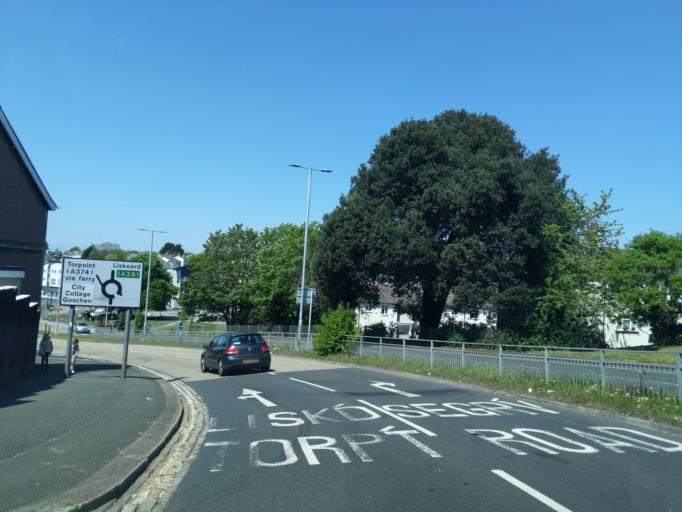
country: GB
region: England
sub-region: Plymouth
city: Plymouth
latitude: 50.3863
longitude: -4.1584
